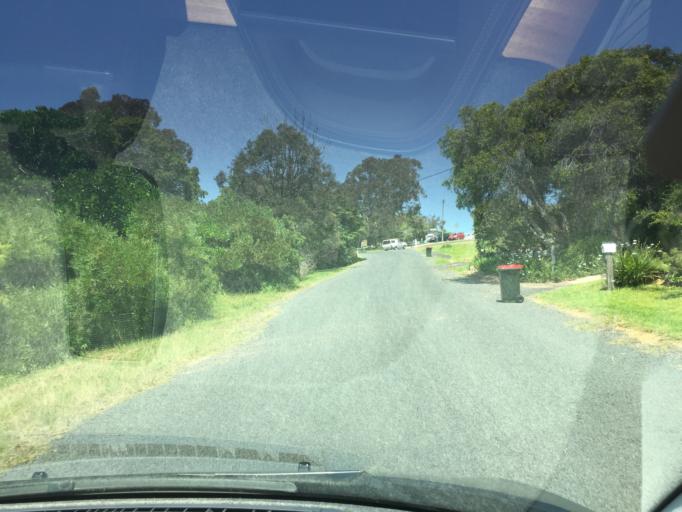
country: AU
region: New South Wales
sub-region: Bega Valley
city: Bega
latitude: -36.7321
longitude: 149.9850
